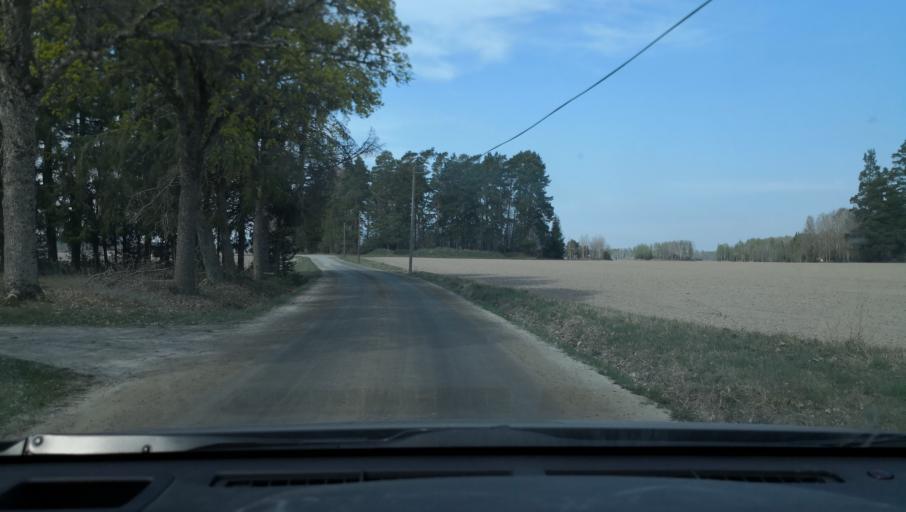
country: SE
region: Vaestmanland
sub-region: Vasteras
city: Skultuna
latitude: 59.7864
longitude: 16.4573
